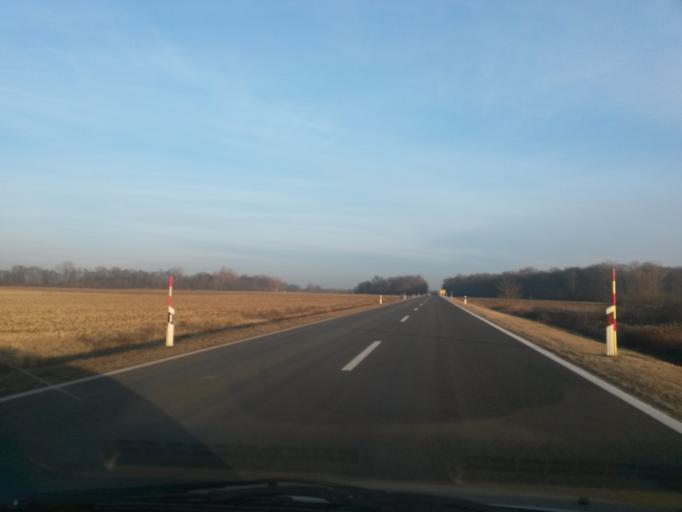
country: HR
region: Varazdinska
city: Jalzabet
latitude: 46.2814
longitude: 16.4965
